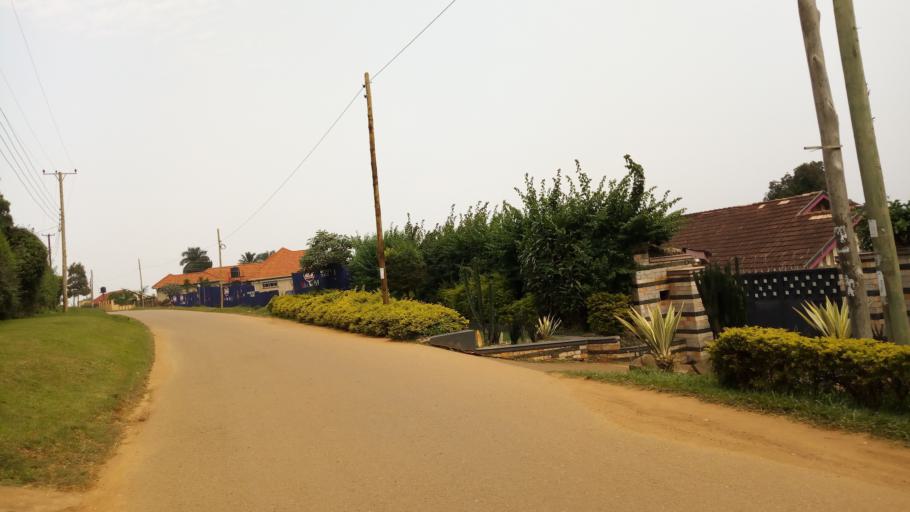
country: UG
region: Central Region
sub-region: Wakiso District
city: Kireka
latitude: 0.3141
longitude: 32.6399
